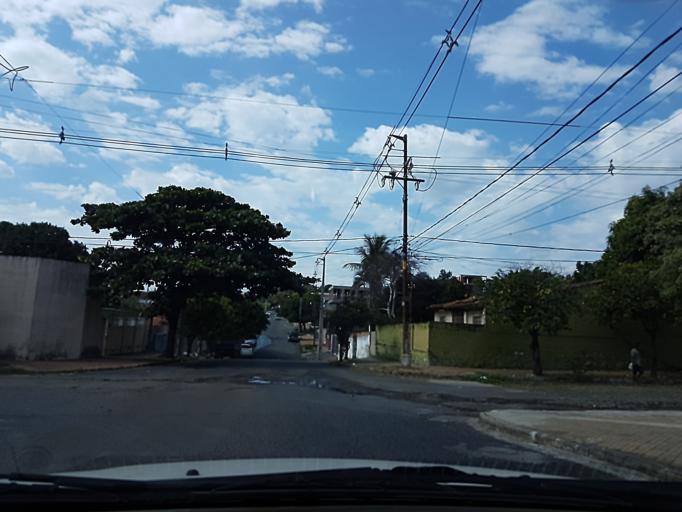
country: PY
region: Asuncion
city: Asuncion
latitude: -25.2753
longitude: -57.6029
